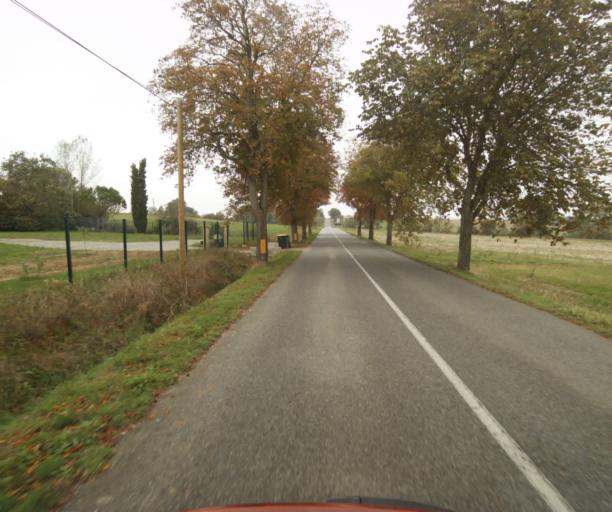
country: FR
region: Midi-Pyrenees
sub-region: Departement du Tarn-et-Garonne
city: Verdun-sur-Garonne
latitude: 43.8058
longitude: 1.2098
